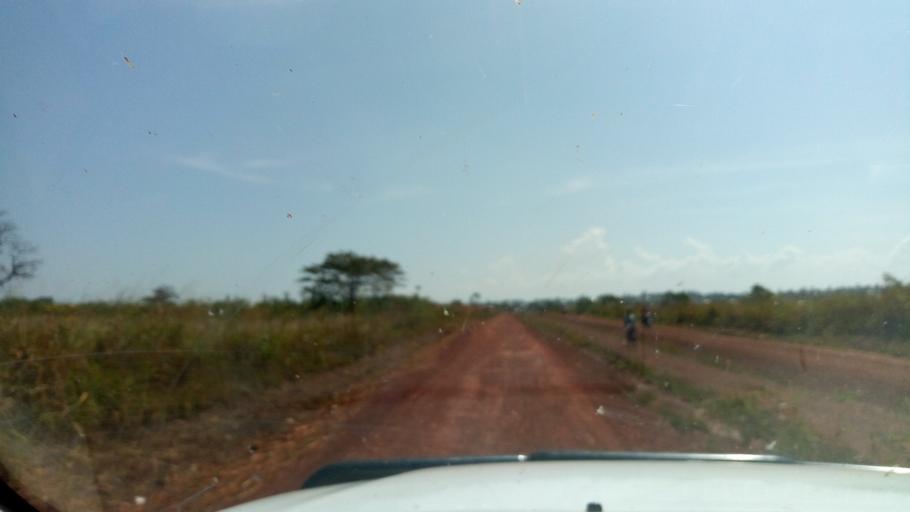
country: UG
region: Western Region
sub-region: Kiryandongo District
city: Kiryandongo
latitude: 1.9503
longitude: 32.1506
